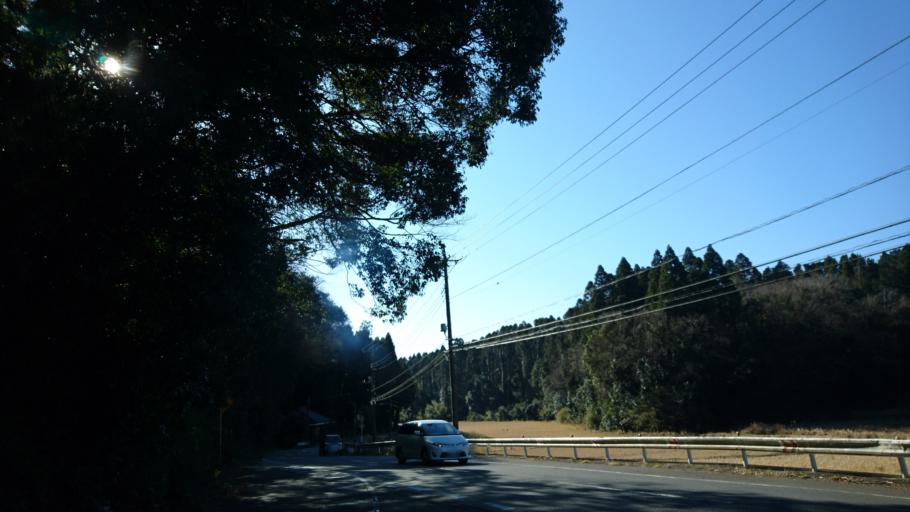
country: JP
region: Chiba
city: Yachimata
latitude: 35.6114
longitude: 140.3462
